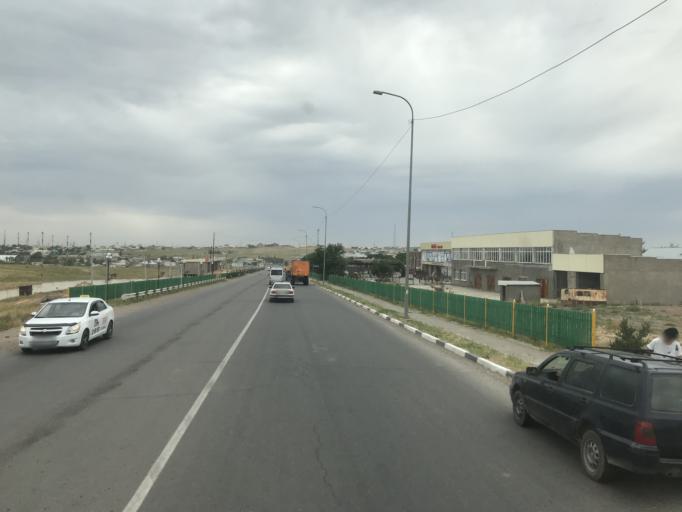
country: KZ
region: Ongtustik Qazaqstan
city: Saryaghash
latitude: 41.4727
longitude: 69.1912
